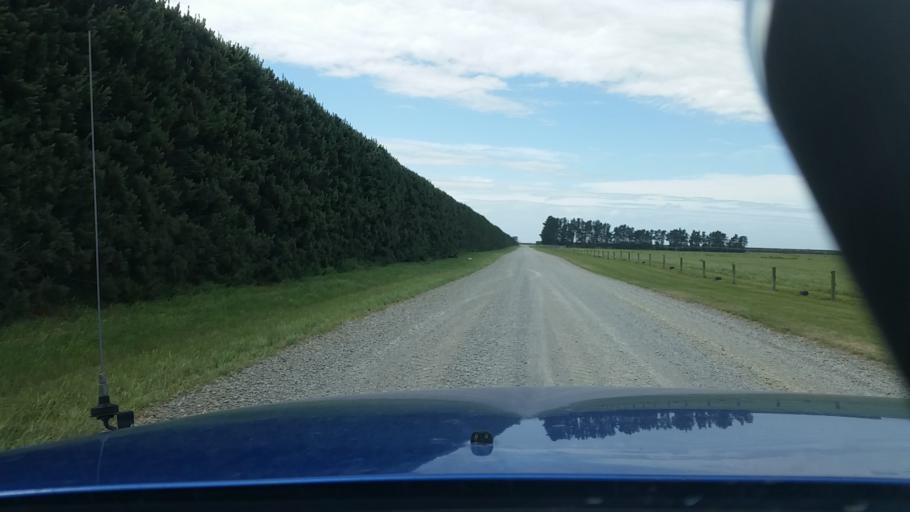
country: NZ
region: Canterbury
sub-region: Ashburton District
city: Ashburton
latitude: -43.9955
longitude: 171.9014
